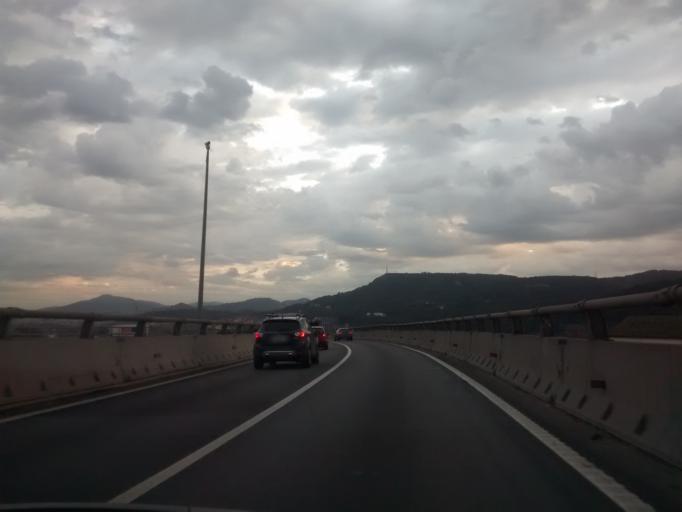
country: ES
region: Catalonia
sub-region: Provincia de Barcelona
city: Palleja
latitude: 41.4420
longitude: 1.9996
